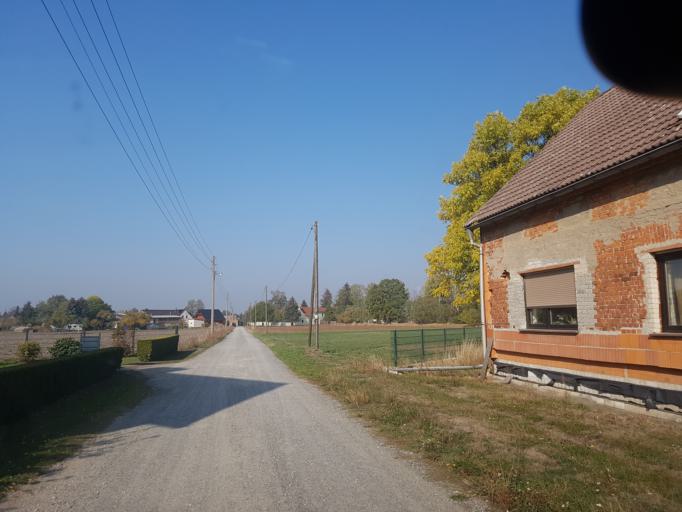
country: DE
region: Brandenburg
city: Finsterwalde
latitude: 51.6101
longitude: 13.7229
